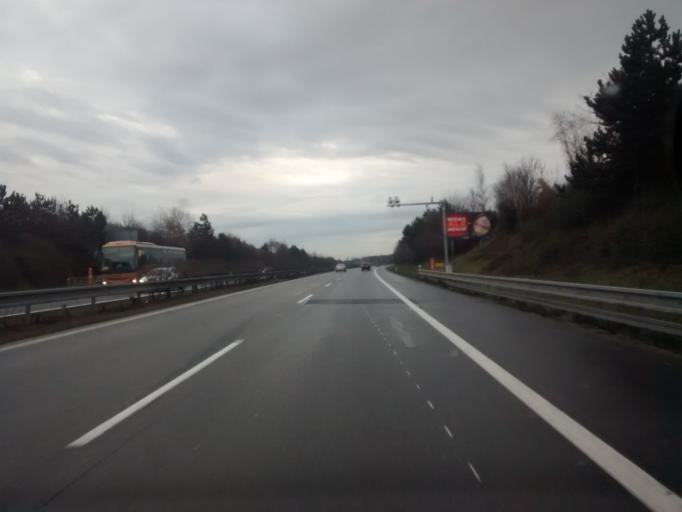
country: CZ
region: Central Bohemia
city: Odolena Voda
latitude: 50.2212
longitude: 14.4160
